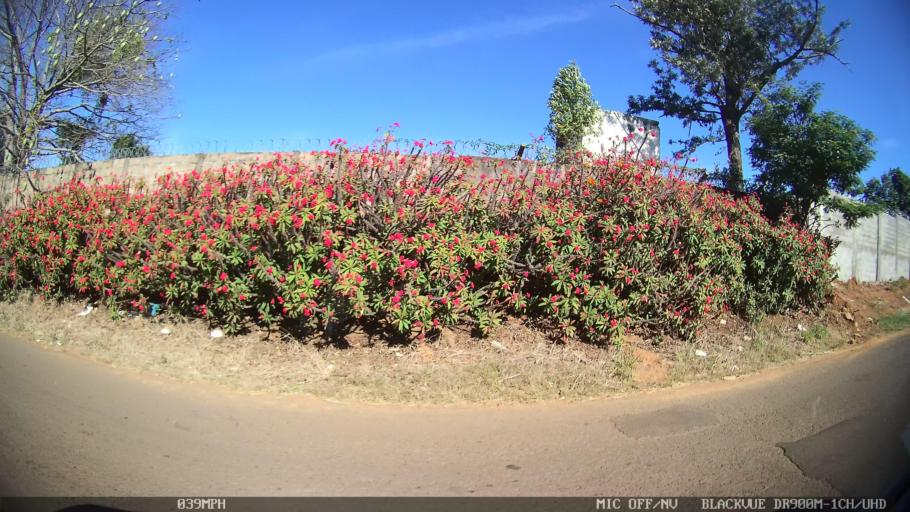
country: BR
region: Sao Paulo
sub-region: Franca
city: Franca
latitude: -20.5693
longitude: -47.3516
